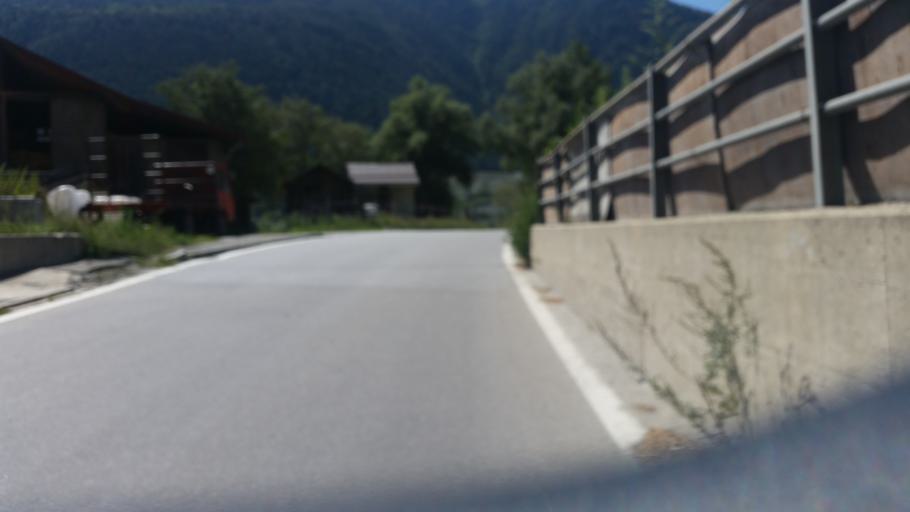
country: CH
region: Valais
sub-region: Raron District
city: Raron
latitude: 46.3075
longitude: 7.8258
